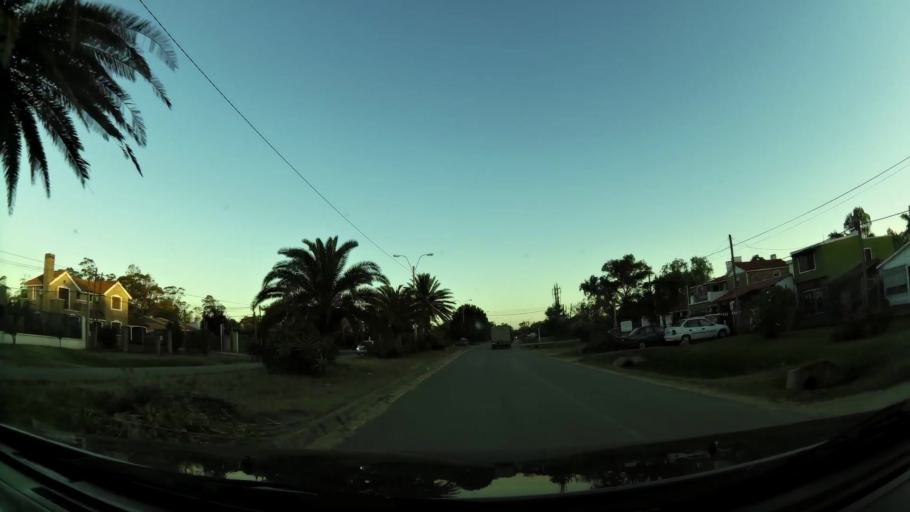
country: UY
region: Canelones
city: Barra de Carrasco
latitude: -34.8489
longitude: -55.9823
